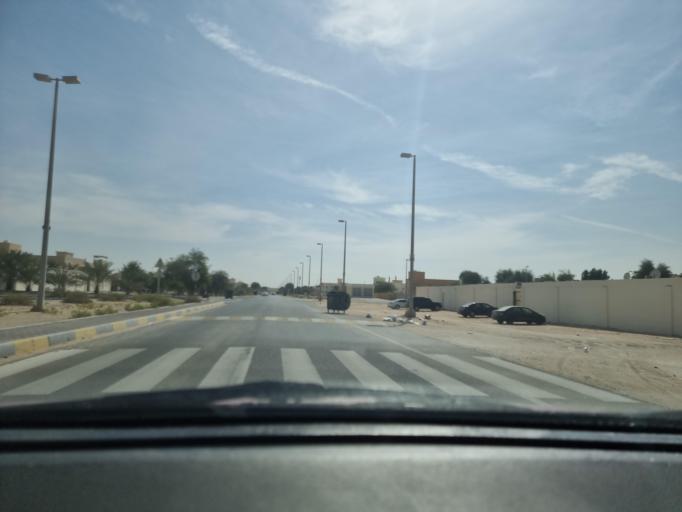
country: AE
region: Abu Dhabi
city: Abu Dhabi
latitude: 24.3838
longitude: 54.6997
